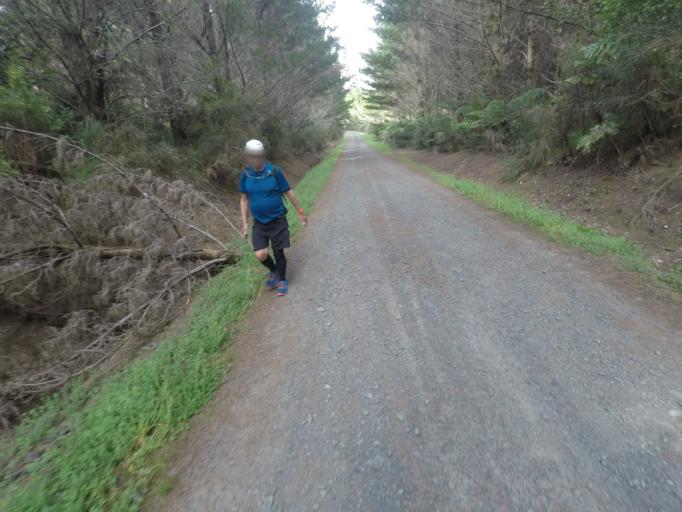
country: NZ
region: Auckland
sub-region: Auckland
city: Muriwai Beach
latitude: -36.7404
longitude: 174.5731
